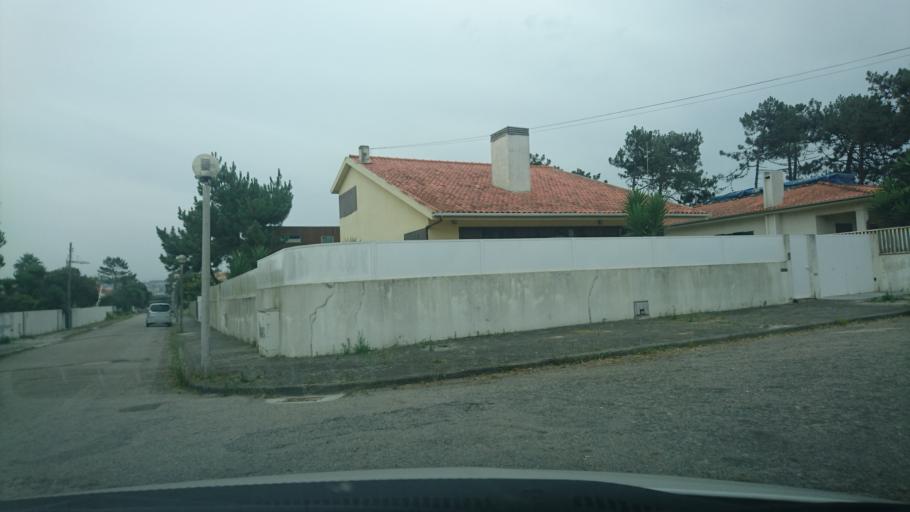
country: PT
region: Aveiro
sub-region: Ovar
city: Esmoriz
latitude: 40.9584
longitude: -8.6483
